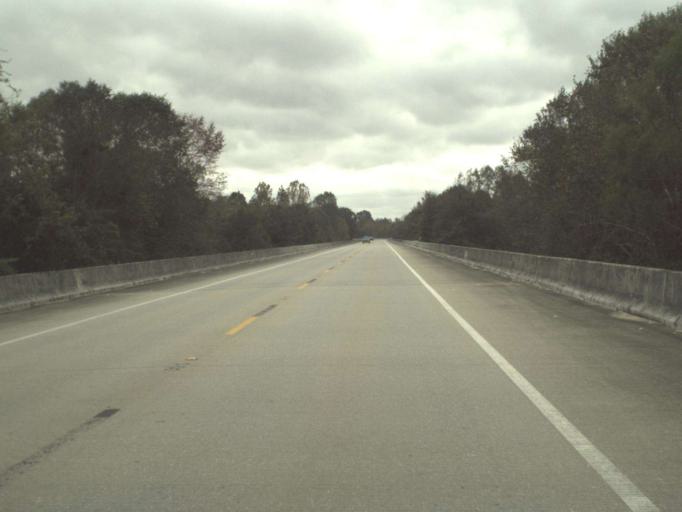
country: US
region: Florida
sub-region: Escambia County
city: Century
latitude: 30.9653
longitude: -87.2366
